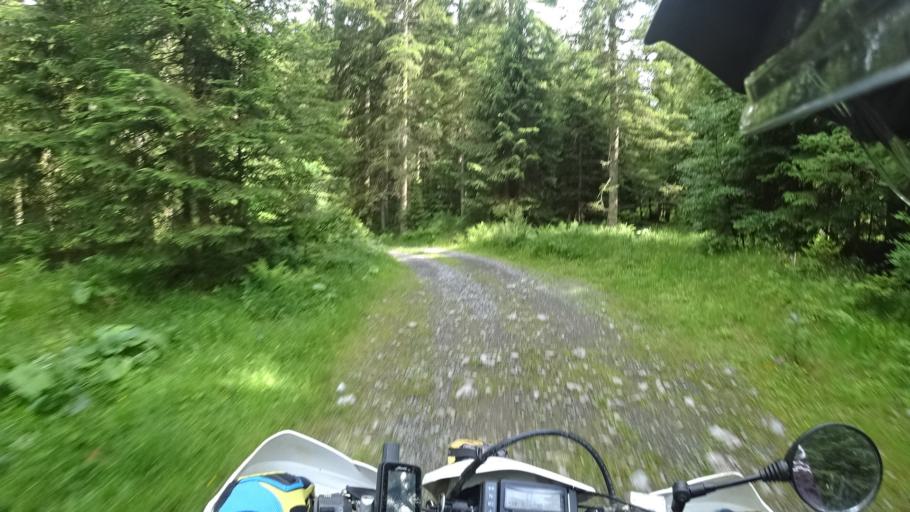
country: HR
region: Primorsko-Goranska
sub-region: Grad Delnice
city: Delnice
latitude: 45.2656
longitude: 14.9033
